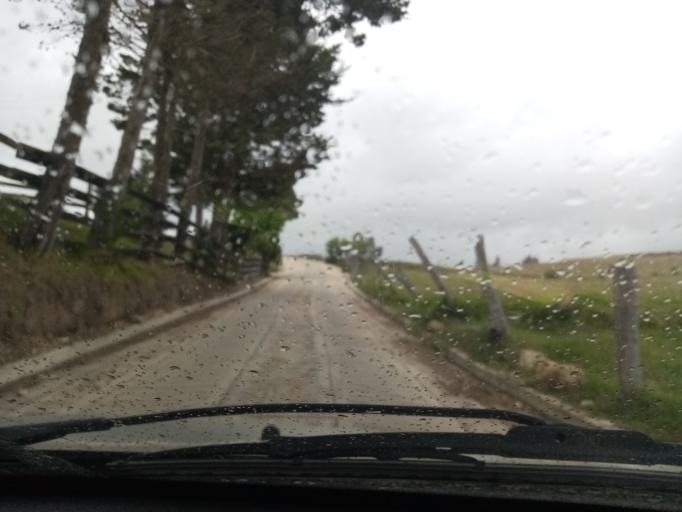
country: CO
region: Boyaca
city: Siachoque
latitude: 5.5582
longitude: -73.2504
